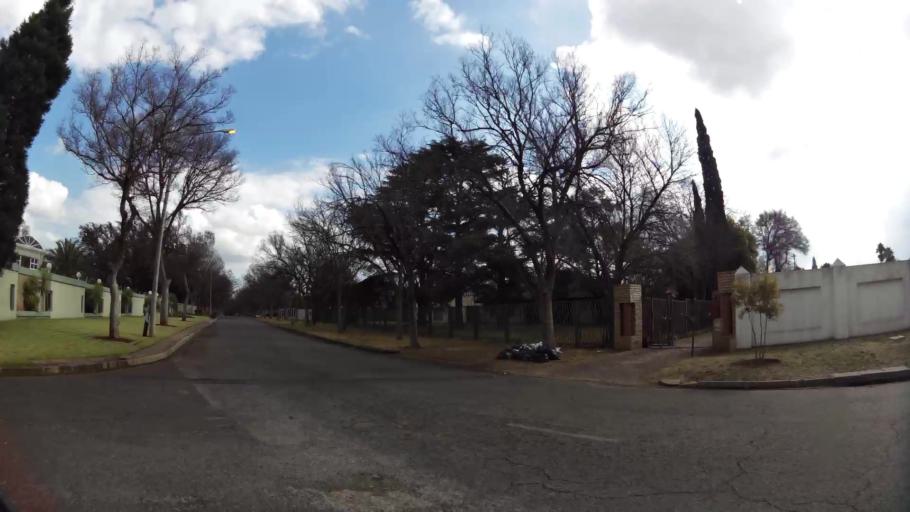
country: ZA
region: Gauteng
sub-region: Sedibeng District Municipality
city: Vanderbijlpark
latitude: -26.7421
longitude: 27.8335
